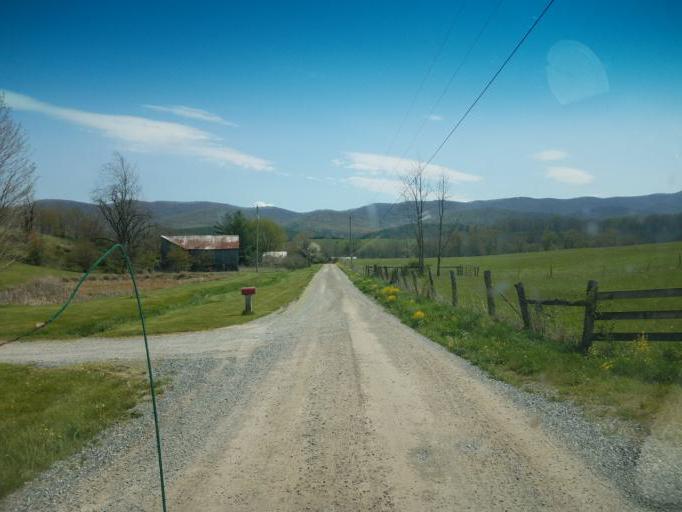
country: US
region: Virginia
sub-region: Smyth County
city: Marion
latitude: 36.7768
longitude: -81.4544
